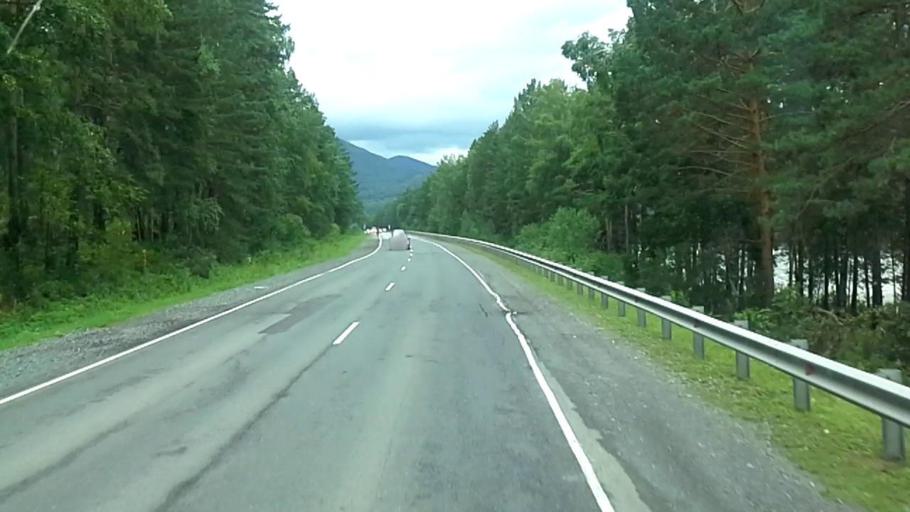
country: RU
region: Altay
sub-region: Mayminskiy Rayon
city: Manzherok
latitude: 51.8106
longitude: 85.7599
